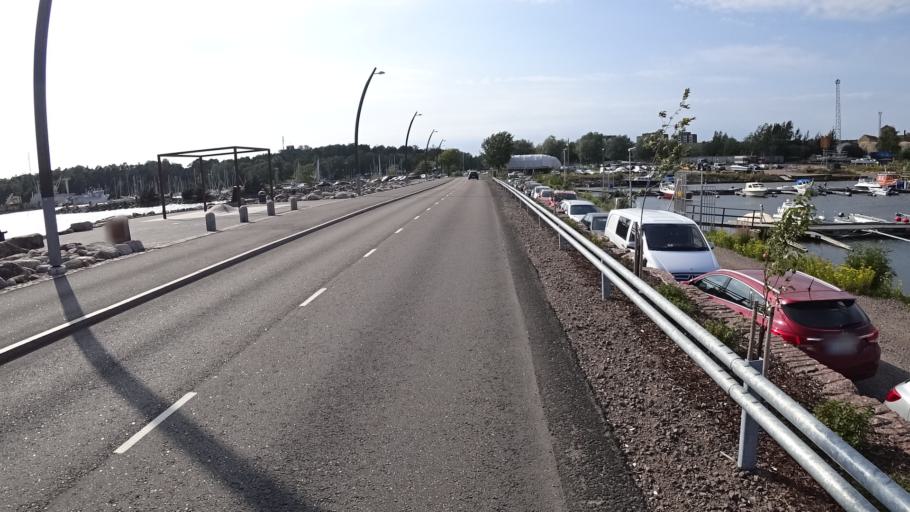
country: FI
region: Kymenlaakso
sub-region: Kotka-Hamina
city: Kotka
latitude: 60.4588
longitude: 26.9585
